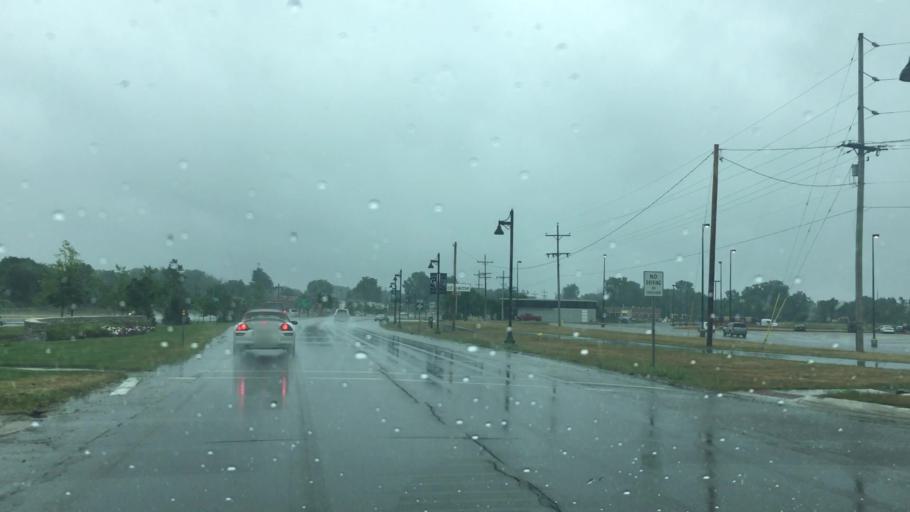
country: US
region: Michigan
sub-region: Ottawa County
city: Jenison
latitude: 42.9031
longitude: -85.7916
